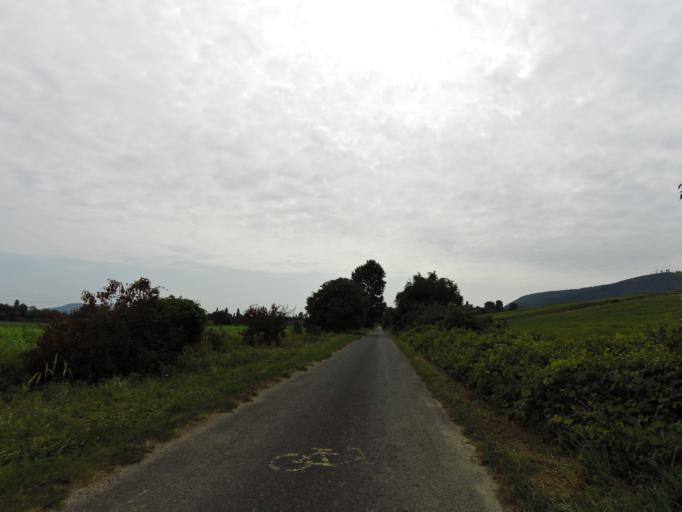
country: HU
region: Veszprem
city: Tapolca
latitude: 46.8433
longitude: 17.3650
